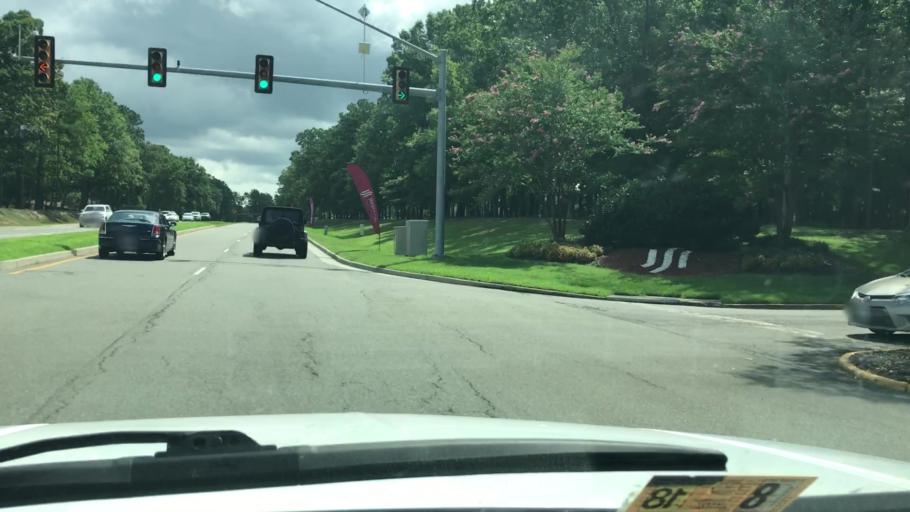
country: US
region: Virginia
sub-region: Henrico County
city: Lakeside
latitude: 37.6386
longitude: -77.4750
